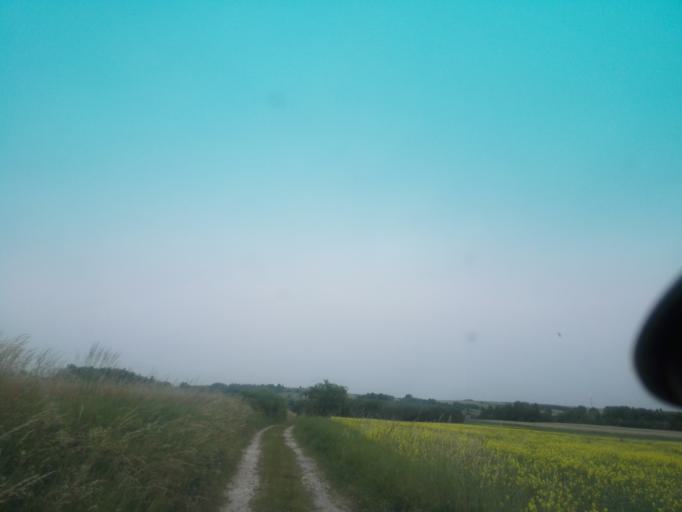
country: PL
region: Silesian Voivodeship
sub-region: Powiat czestochowski
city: Mstow
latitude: 50.7904
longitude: 19.3616
